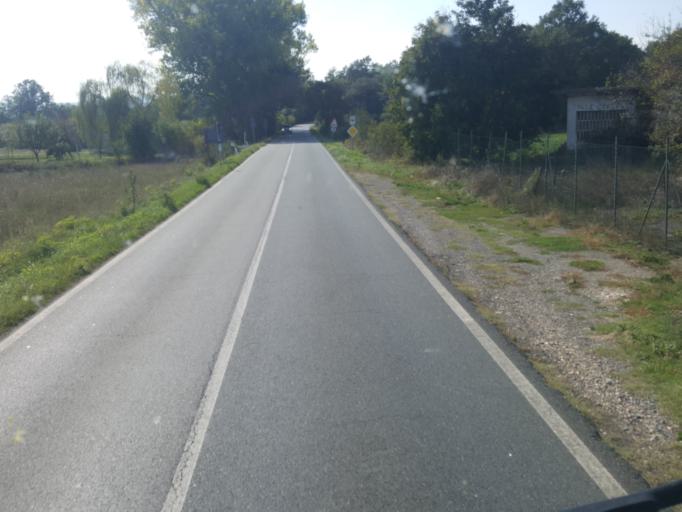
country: IT
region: Tuscany
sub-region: Provincia di Siena
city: Colle di Val d'Elsa
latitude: 43.3855
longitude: 11.0855
